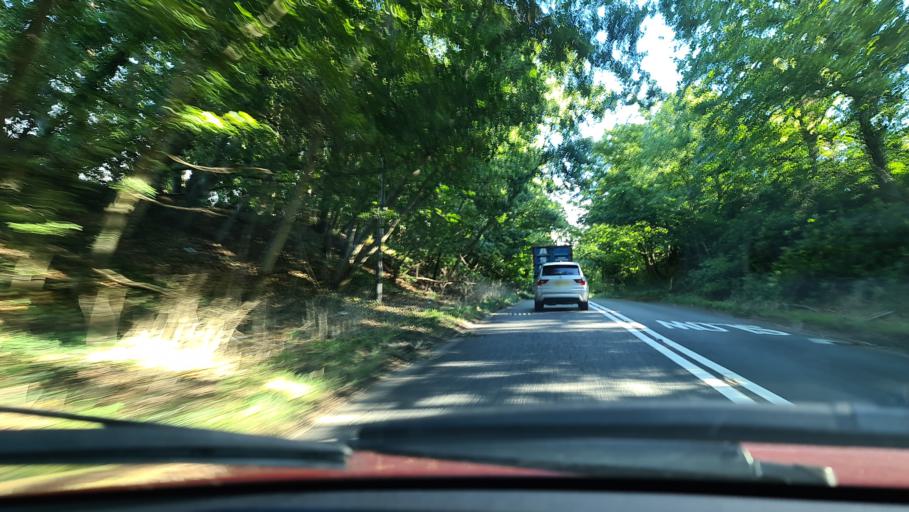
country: GB
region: England
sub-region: Buckinghamshire
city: Beaconsfield
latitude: 51.6176
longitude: -0.6299
